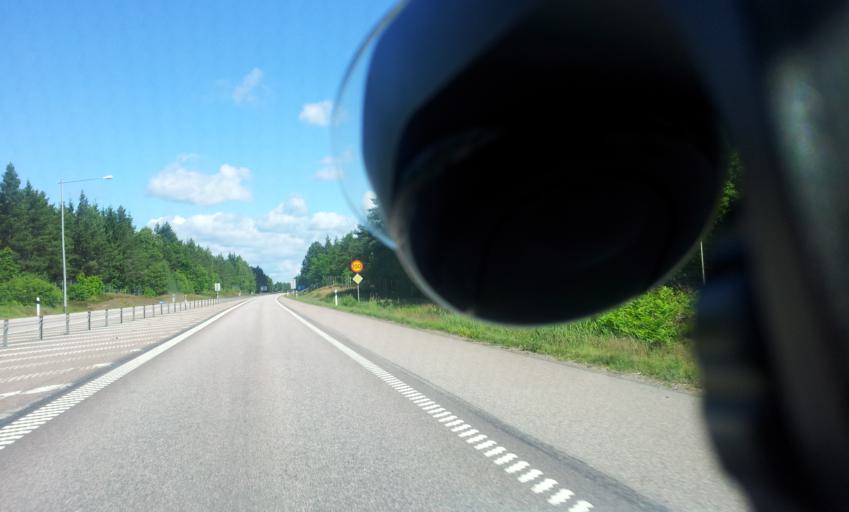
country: SE
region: Kalmar
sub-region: Oskarshamns Kommun
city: Paskallavik
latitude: 57.1967
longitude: 16.4379
